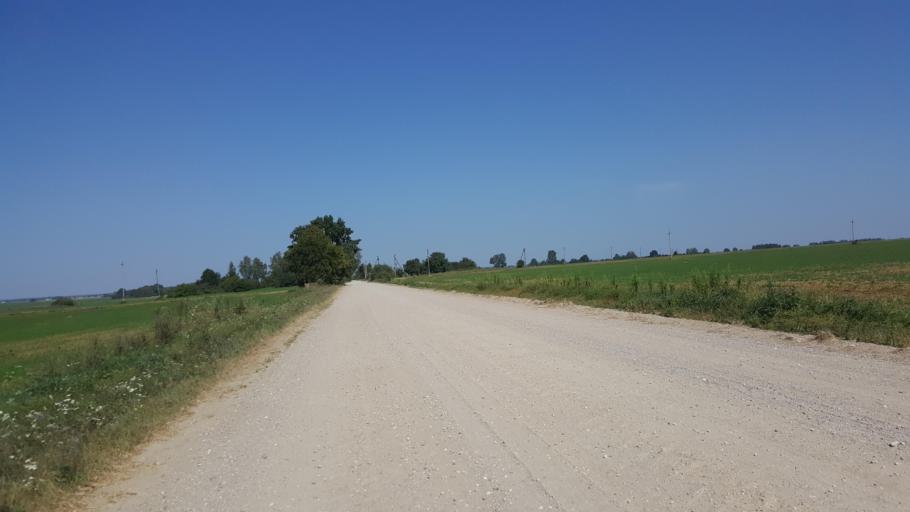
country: PL
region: Podlasie
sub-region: Powiat hajnowski
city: Czeremcha
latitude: 52.4592
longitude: 23.4477
